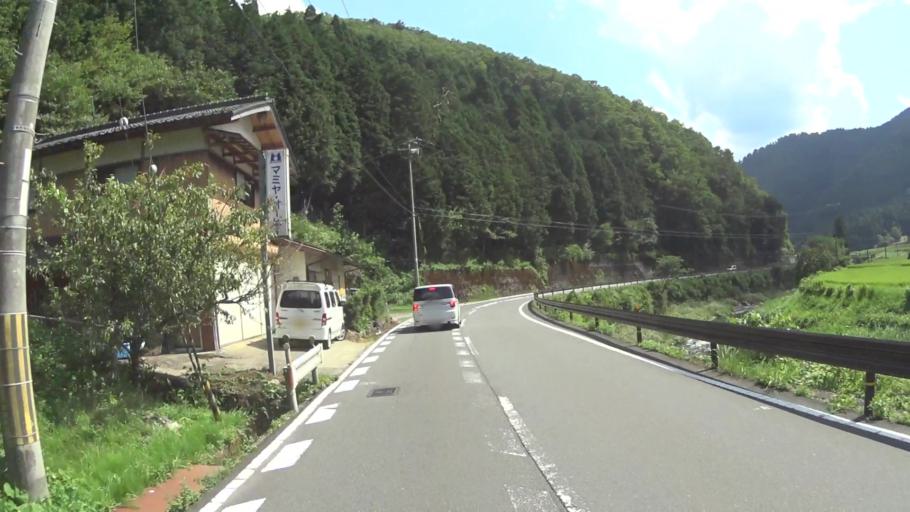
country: JP
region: Kyoto
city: Maizuru
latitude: 35.3024
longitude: 135.5583
